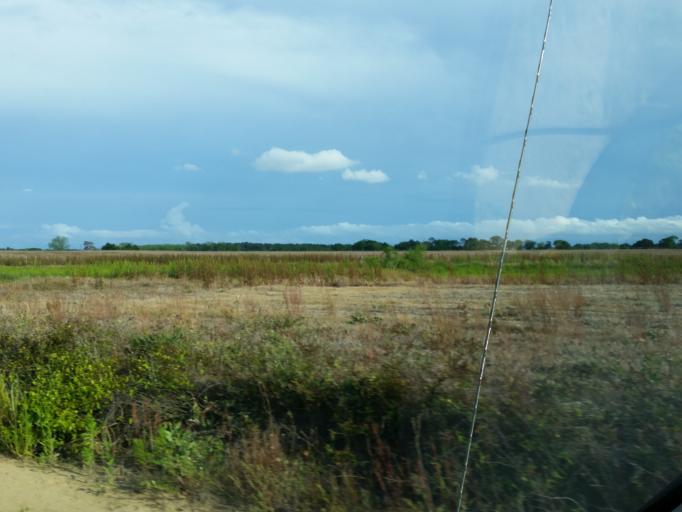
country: US
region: Georgia
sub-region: Dooly County
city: Vienna
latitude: 32.0377
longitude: -83.7797
